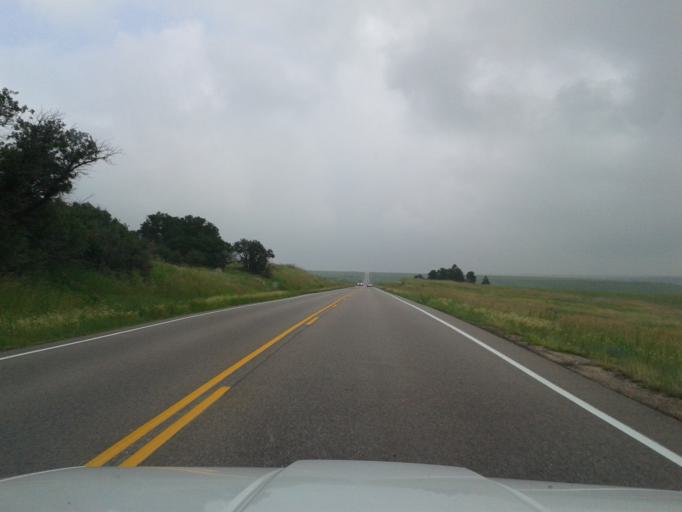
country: US
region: Colorado
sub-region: Douglas County
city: Castle Rock
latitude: 39.2887
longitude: -104.7364
